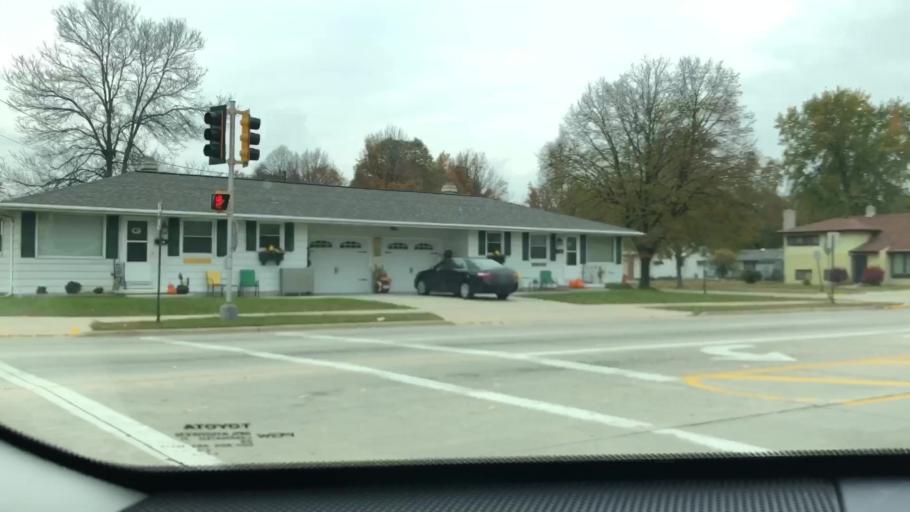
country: US
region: Wisconsin
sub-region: Brown County
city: Ashwaubenon
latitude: 44.5018
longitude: -88.0567
